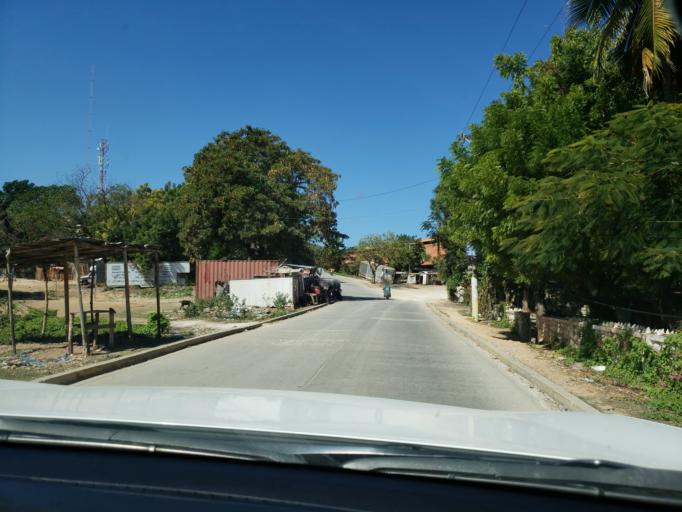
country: HT
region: Nippes
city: Miragoane
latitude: 18.4475
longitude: -73.1071
